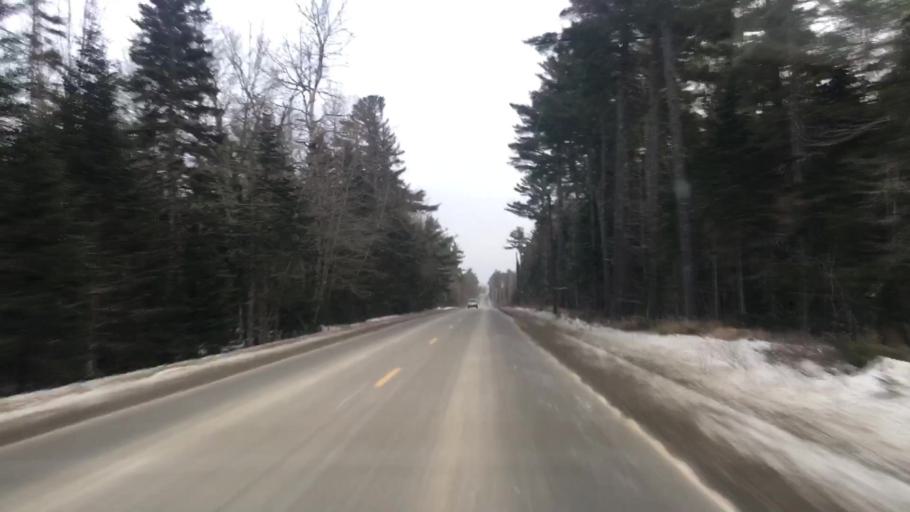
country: US
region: Maine
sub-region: Hancock County
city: Ellsworth
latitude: 44.6735
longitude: -68.3538
